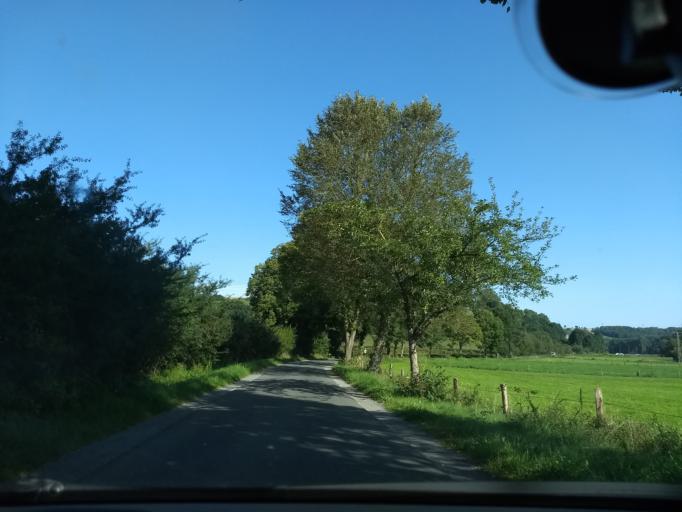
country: DE
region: North Rhine-Westphalia
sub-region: Regierungsbezirk Detmold
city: Buren
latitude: 51.5283
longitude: 8.5251
